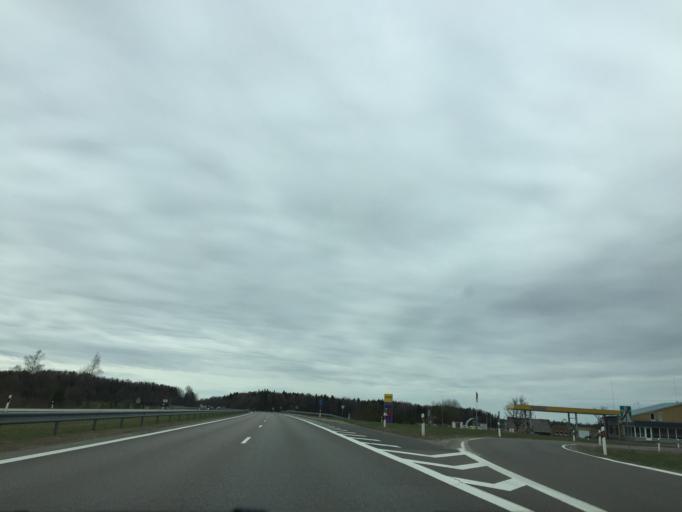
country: LT
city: Rietavas
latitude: 55.6860
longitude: 21.6942
